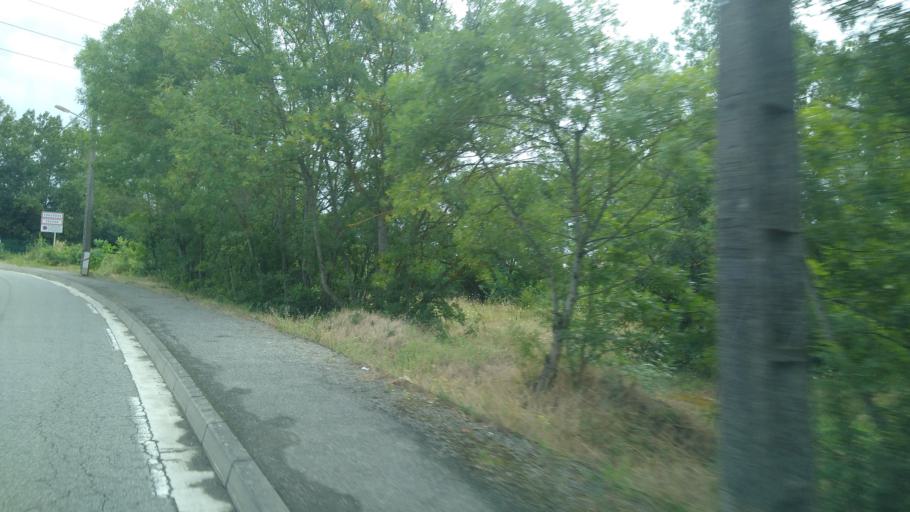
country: FR
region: Midi-Pyrenees
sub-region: Departement de la Haute-Garonne
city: Blagnac
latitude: 43.5990
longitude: 1.3721
